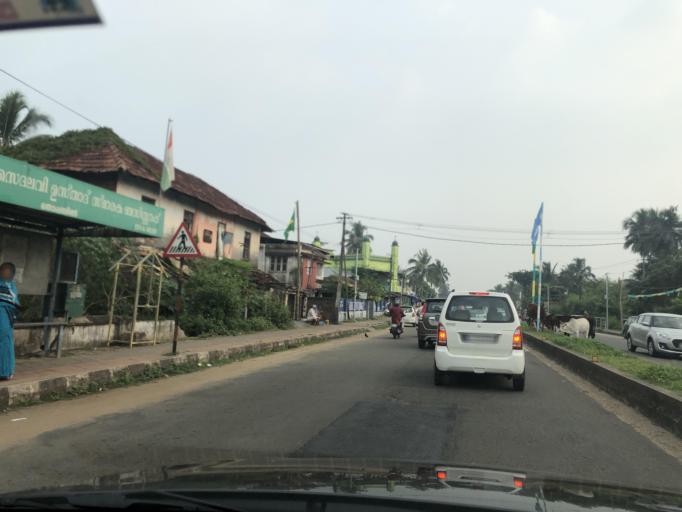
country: IN
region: Kerala
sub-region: Kozhikode
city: Kozhikode
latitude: 11.2720
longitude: 75.7653
